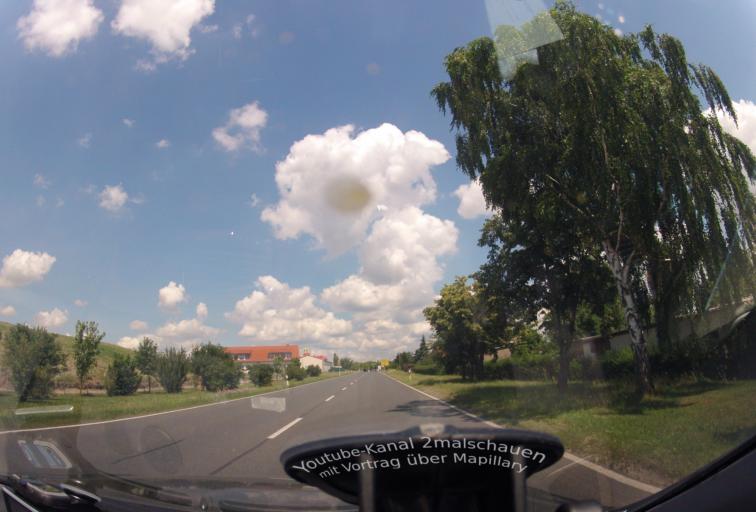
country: DE
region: Saxony
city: Zinna
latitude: 51.5592
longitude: 12.9697
